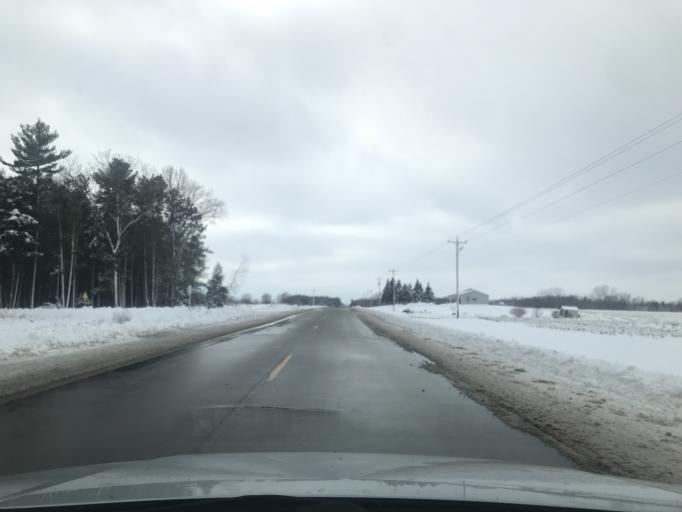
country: US
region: Wisconsin
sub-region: Oconto County
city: Oconto
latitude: 44.9501
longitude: -87.9787
